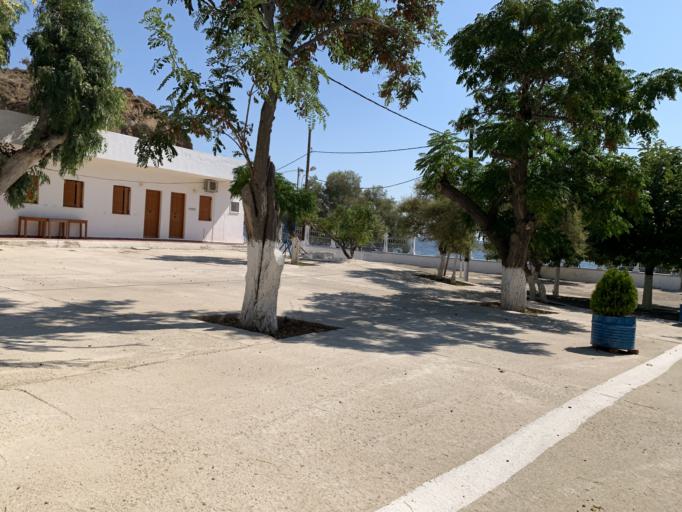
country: GR
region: North Aegean
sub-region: Chios
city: Vrontados
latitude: 38.4798
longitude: 25.8874
